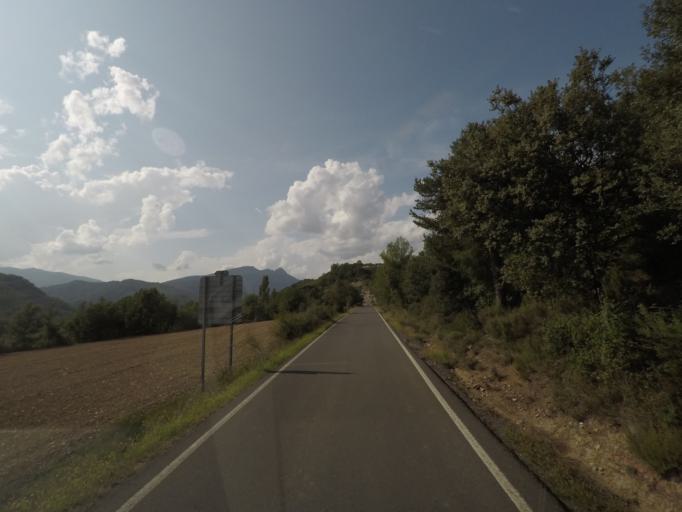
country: ES
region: Aragon
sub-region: Provincia de Huesca
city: Laspuna
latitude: 42.5013
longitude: 0.1408
